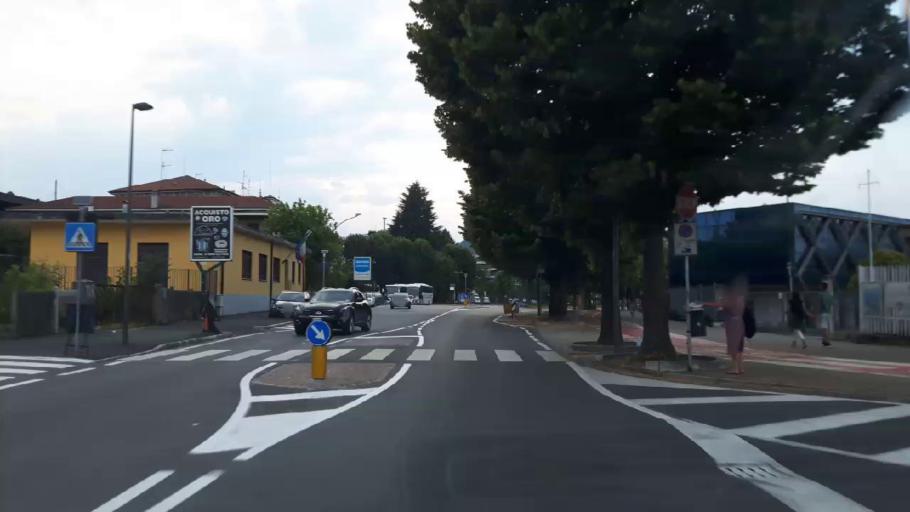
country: IT
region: Piedmont
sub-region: Provincia di Novara
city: Arona
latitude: 45.7549
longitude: 8.5608
